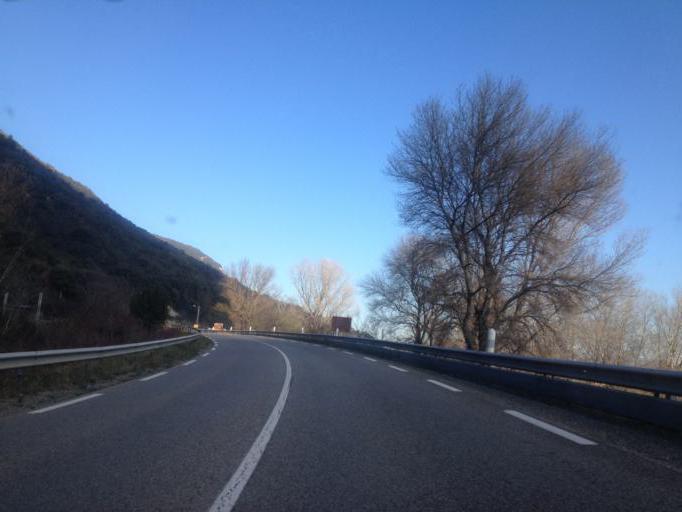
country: FR
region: Rhone-Alpes
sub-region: Departement de l'Ardeche
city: Cruas
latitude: 44.6469
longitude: 4.7561
